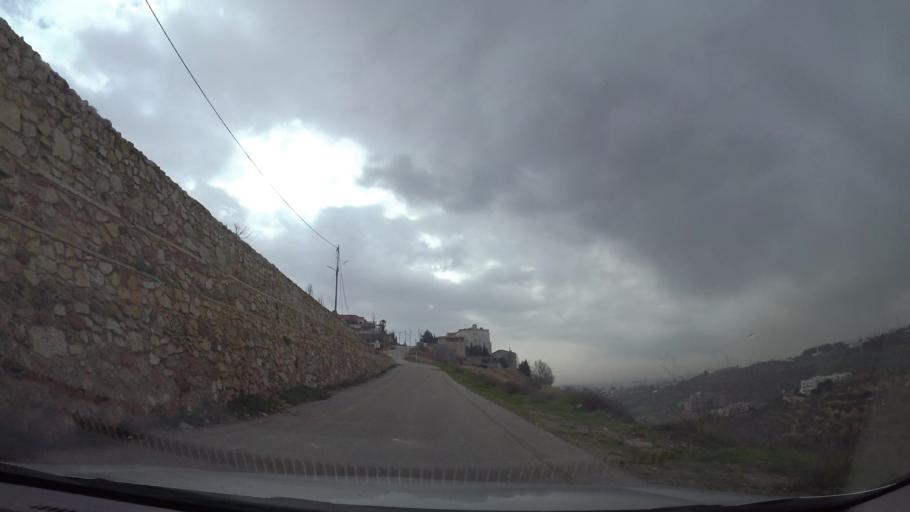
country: JO
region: Amman
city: Wadi as Sir
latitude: 31.9868
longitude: 35.8160
